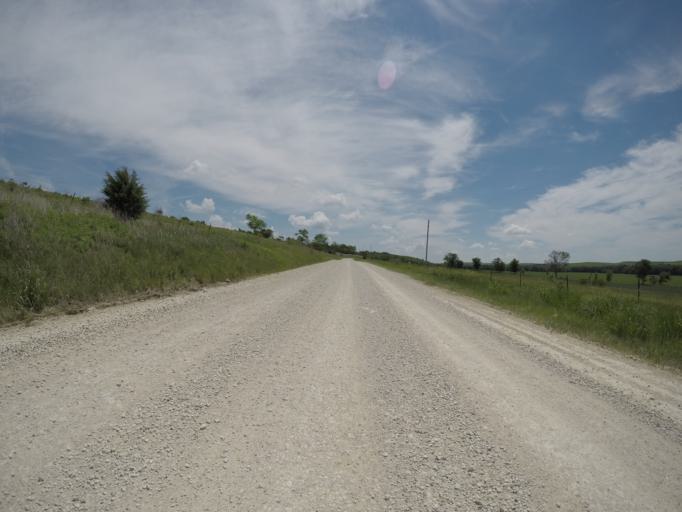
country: US
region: Kansas
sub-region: Wabaunsee County
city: Alma
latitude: 38.9439
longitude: -96.2381
